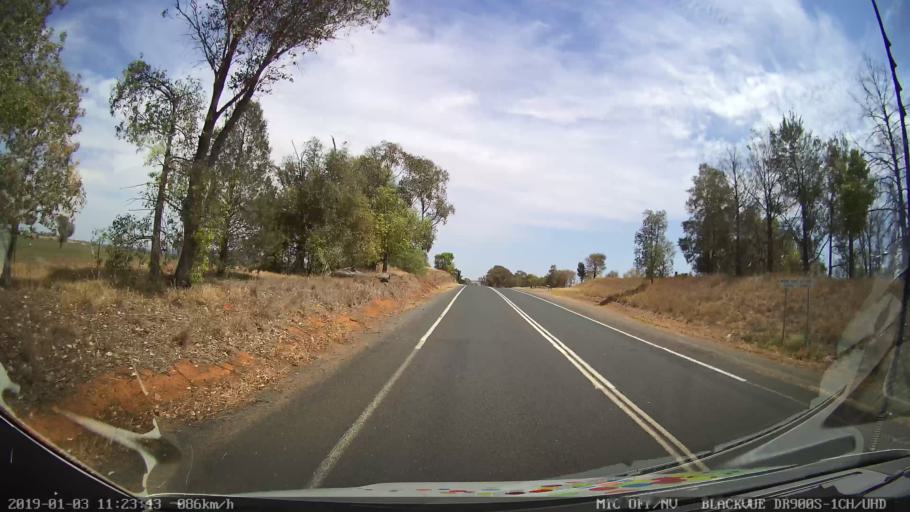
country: AU
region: New South Wales
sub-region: Weddin
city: Grenfell
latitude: -34.0600
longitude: 148.2405
